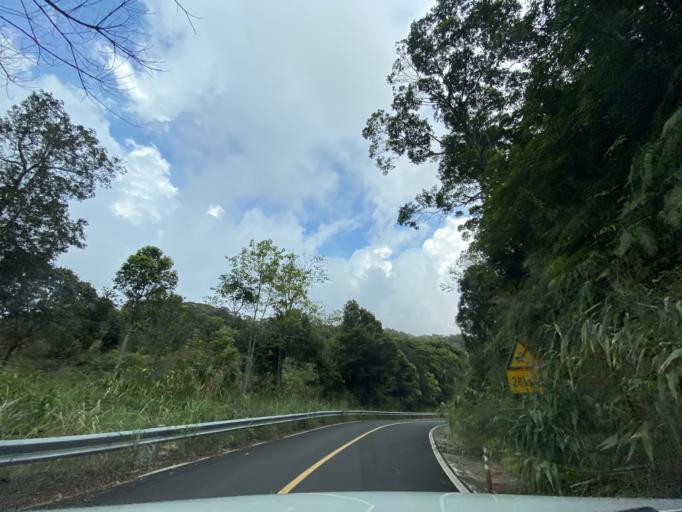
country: CN
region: Hainan
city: Diaoluoshan
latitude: 18.7188
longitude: 109.8782
